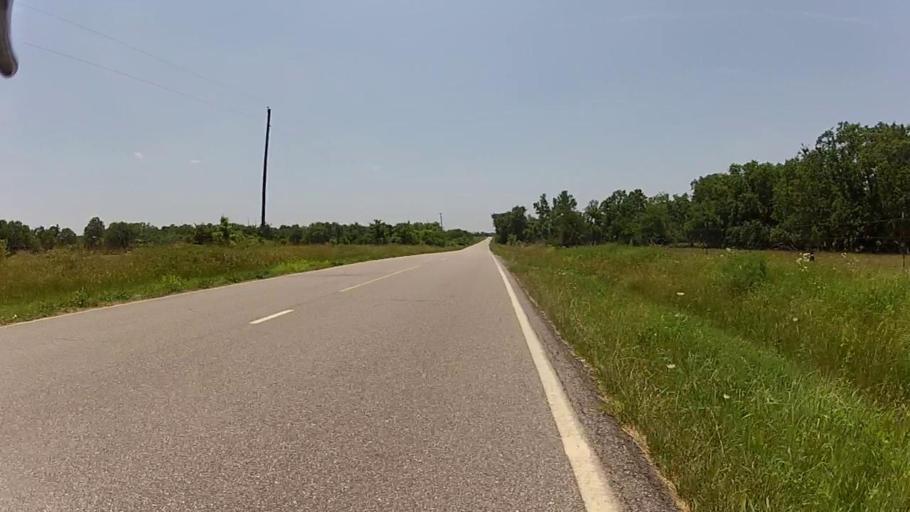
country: US
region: Kansas
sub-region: Montgomery County
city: Cherryvale
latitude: 37.2315
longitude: -95.5379
